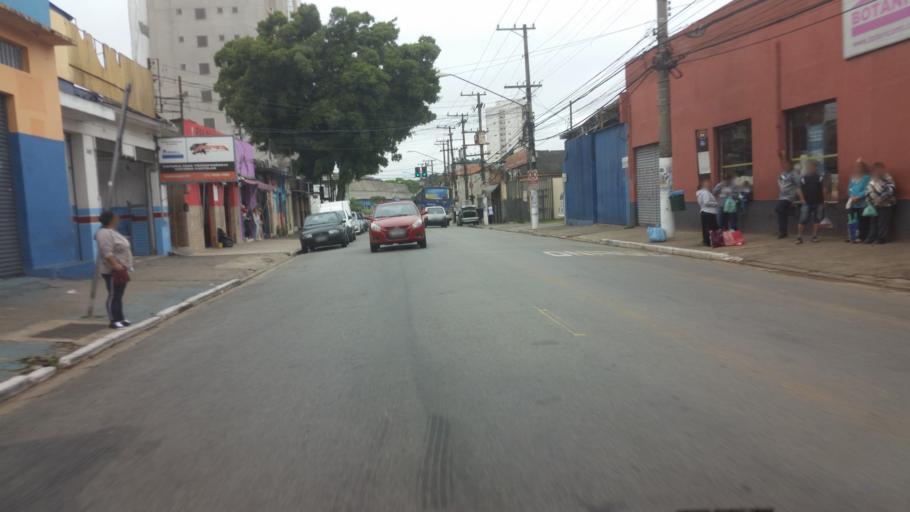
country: BR
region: Sao Paulo
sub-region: Diadema
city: Diadema
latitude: -23.6344
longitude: -46.6274
